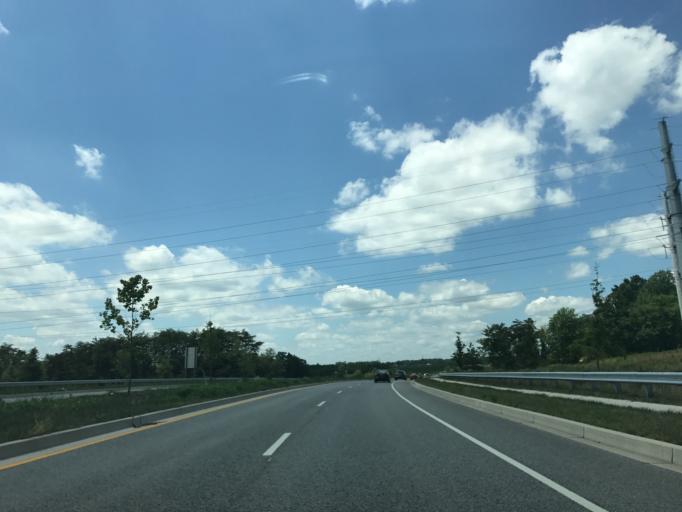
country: US
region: Maryland
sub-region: Prince George's County
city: West Laurel
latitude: 39.0871
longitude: -76.9059
